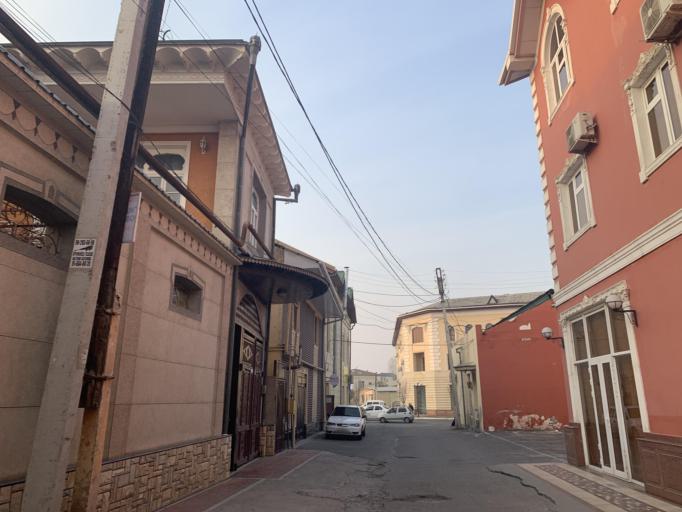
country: UZ
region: Fergana
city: Qo`qon
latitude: 40.5362
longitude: 70.9331
